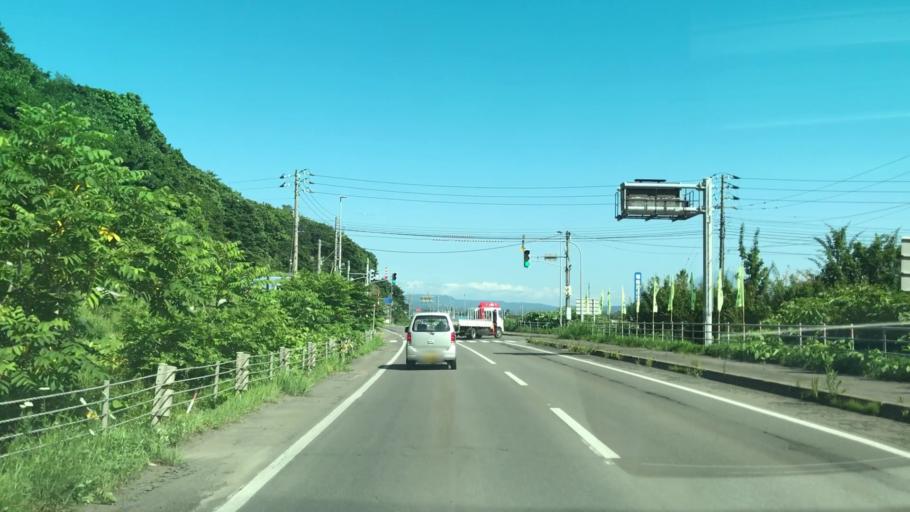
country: JP
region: Hokkaido
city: Iwanai
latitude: 43.0345
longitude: 140.5287
